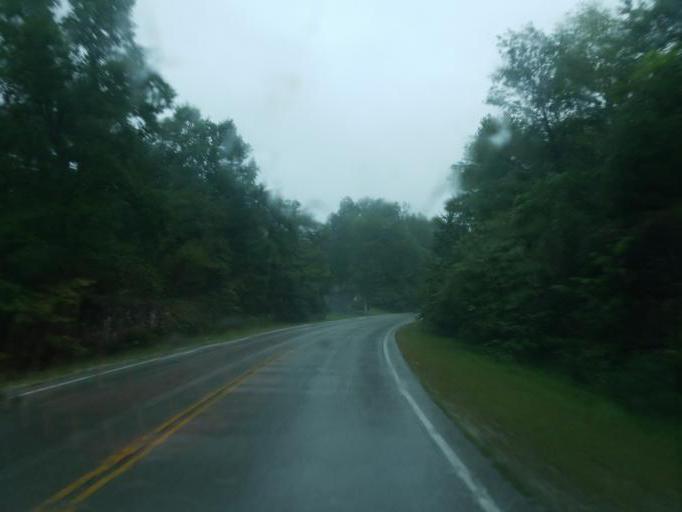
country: US
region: Kentucky
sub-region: Carter County
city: Olive Hill
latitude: 38.3343
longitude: -83.2082
